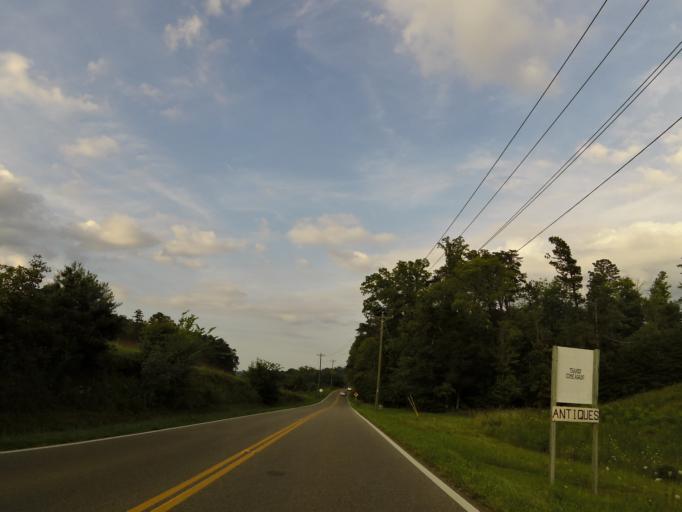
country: US
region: Tennessee
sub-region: Jefferson County
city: Dandridge
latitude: 35.9094
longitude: -83.3952
